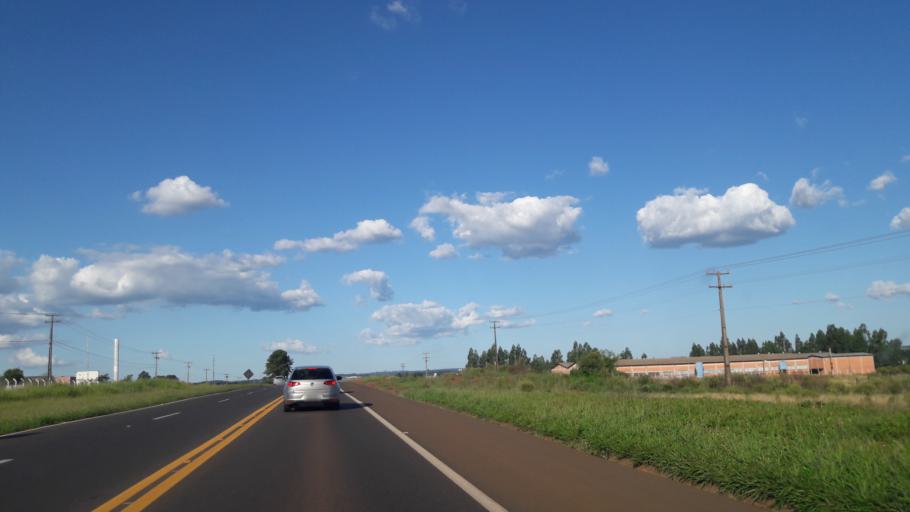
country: BR
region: Parana
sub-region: Guarapuava
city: Guarapuava
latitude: -25.3821
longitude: -51.5107
